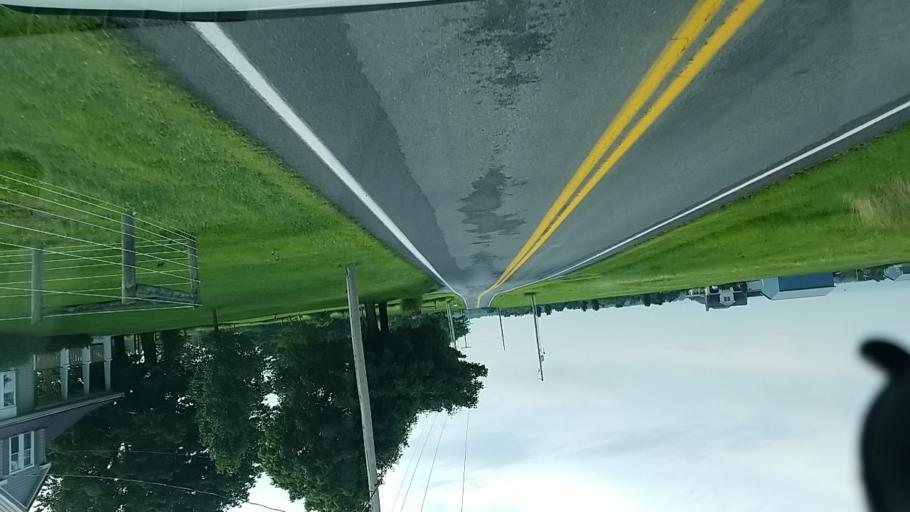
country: US
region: Pennsylvania
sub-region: Cumberland County
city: Newville
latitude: 40.2311
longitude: -77.4534
